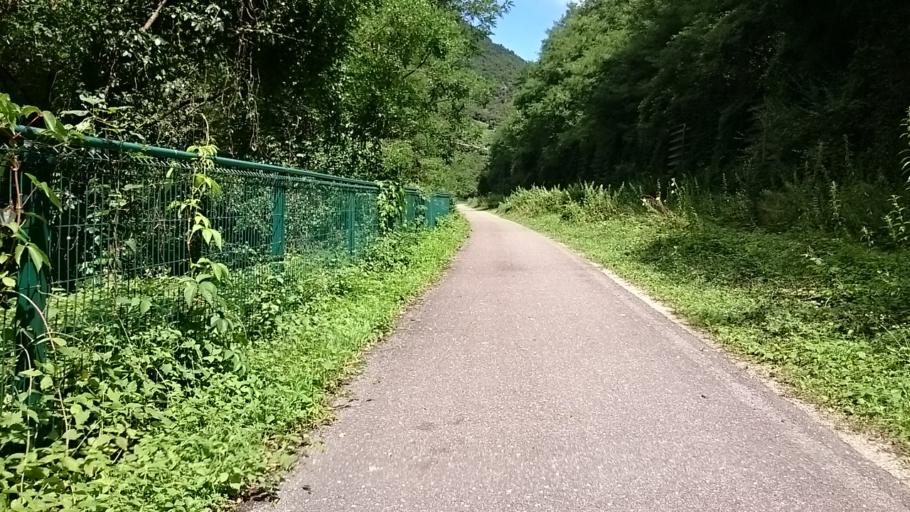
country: IT
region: Trentino-Alto Adige
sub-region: Bolzano
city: Fie Allo Sciliar
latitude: 46.5136
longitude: 11.4786
